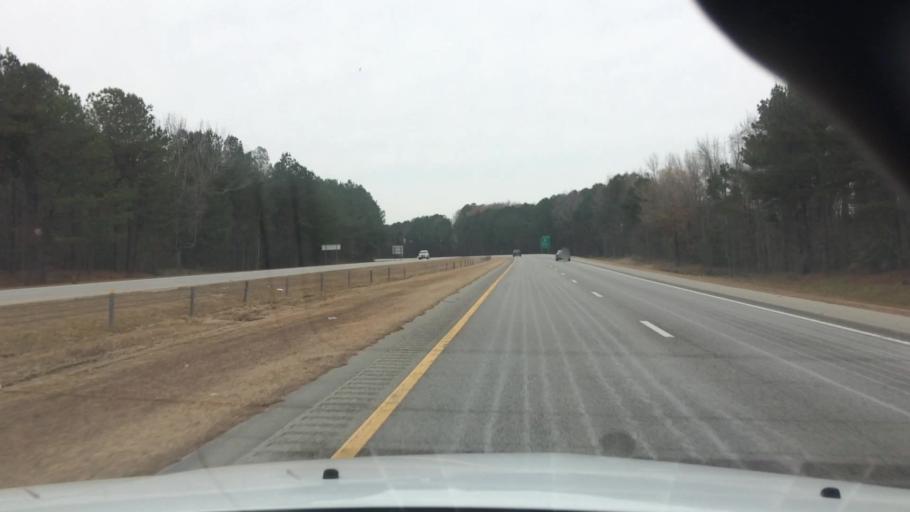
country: US
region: North Carolina
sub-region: Wilson County
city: Wilson
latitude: 35.6760
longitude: -77.8347
